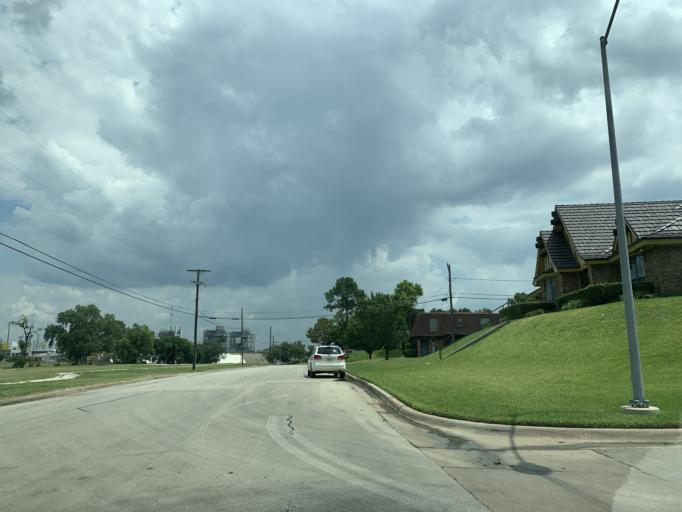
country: US
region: Texas
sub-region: Tarrant County
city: Forest Hill
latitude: 32.7289
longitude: -97.2288
